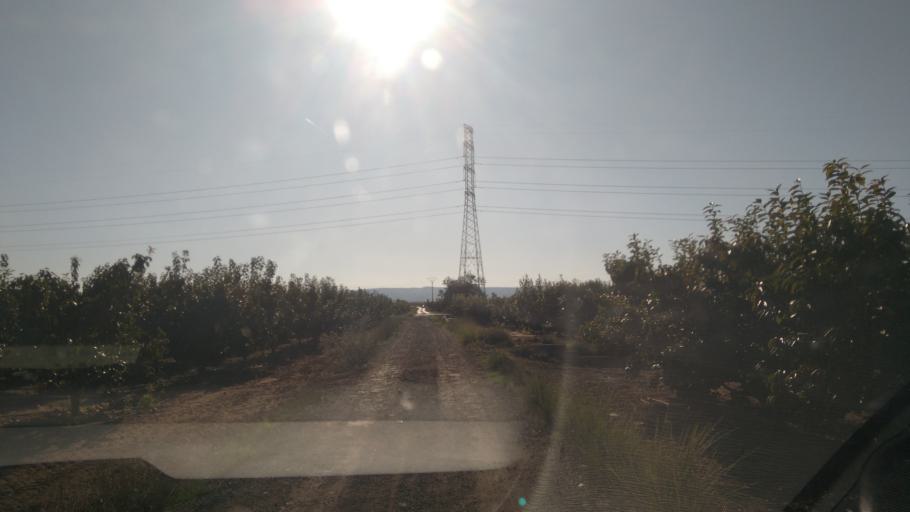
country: ES
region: Valencia
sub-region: Provincia de Valencia
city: L'Alcudia
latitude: 39.1858
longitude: -0.5205
